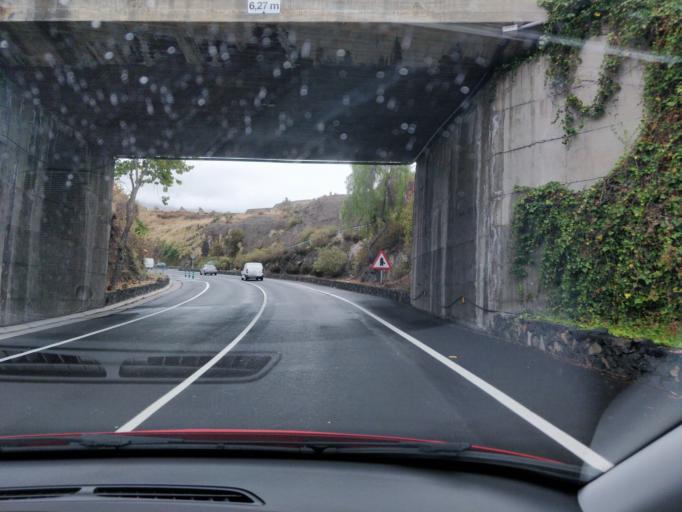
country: ES
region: Canary Islands
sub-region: Provincia de Santa Cruz de Tenerife
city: Puerto de la Cruz
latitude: 28.4085
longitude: -16.5328
